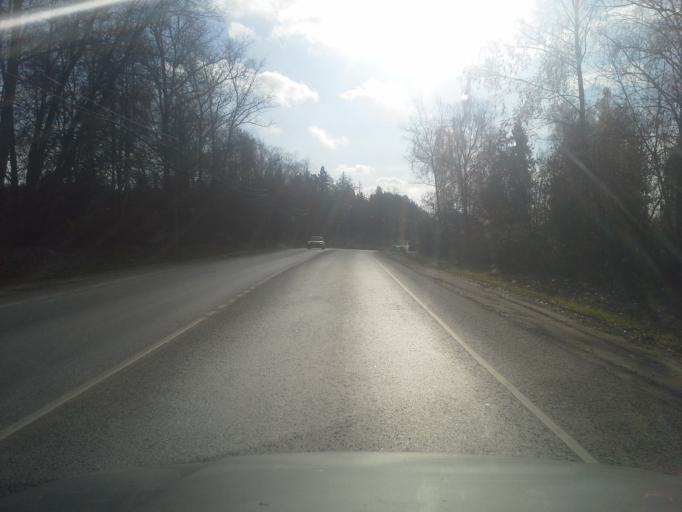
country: RU
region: Moskovskaya
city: Bol'shiye Vyazemy
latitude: 55.6603
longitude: 36.9668
